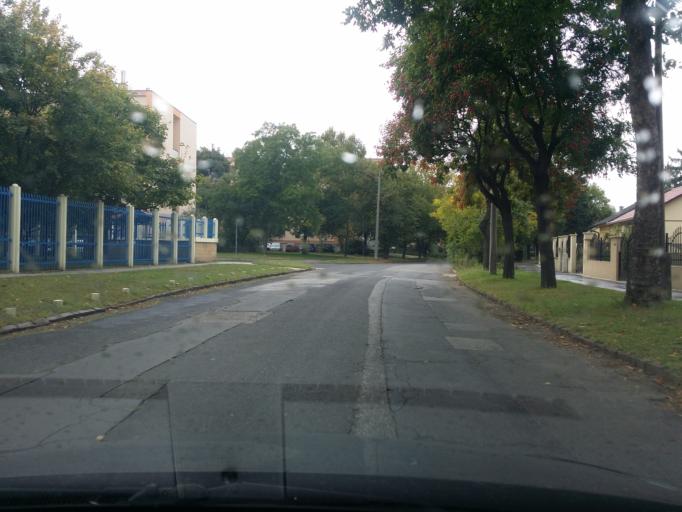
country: HU
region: Budapest
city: Budapest XXI. keruelet
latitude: 47.4086
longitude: 19.0645
